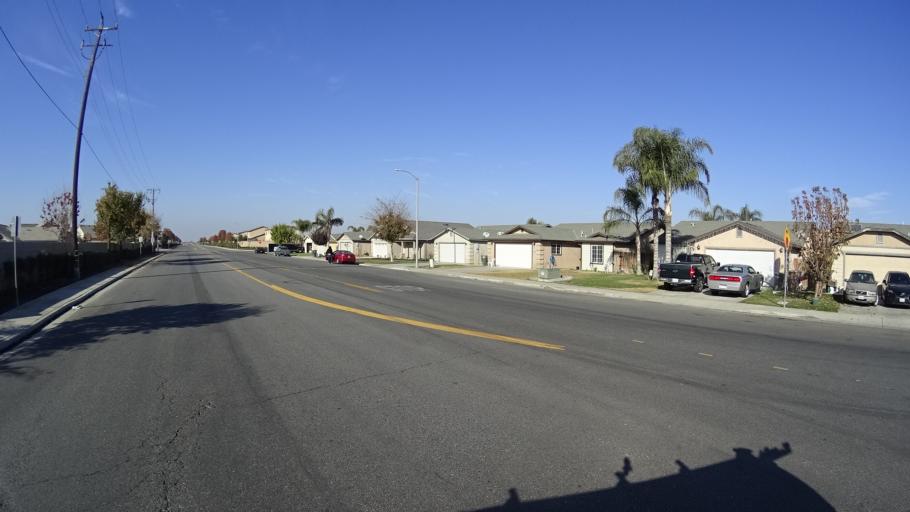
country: US
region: California
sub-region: Kern County
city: Greenfield
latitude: 35.2742
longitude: -119.0642
